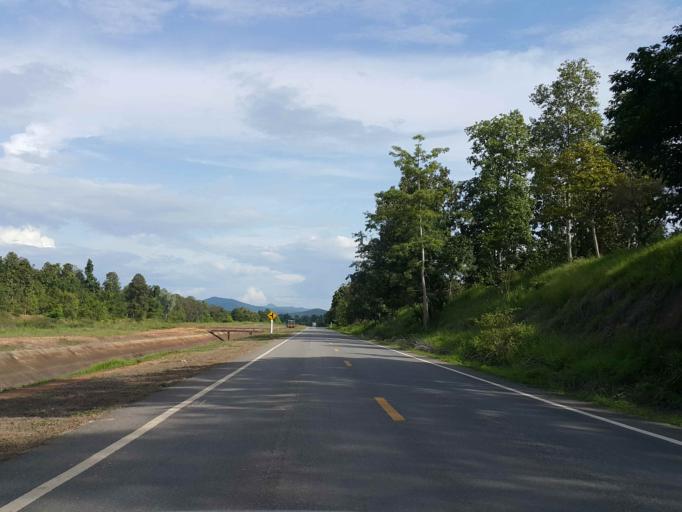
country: TH
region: Chiang Mai
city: San Sai
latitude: 18.8939
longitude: 99.1504
